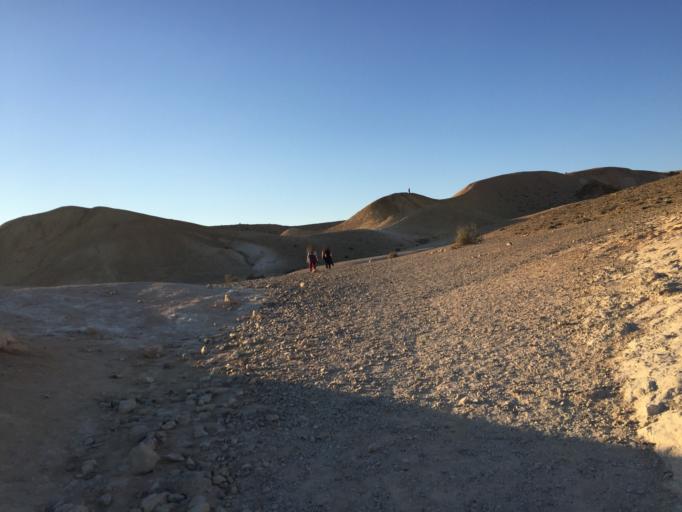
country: IL
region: Southern District
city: Midreshet Ben-Gurion
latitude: 30.8443
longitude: 34.7572
